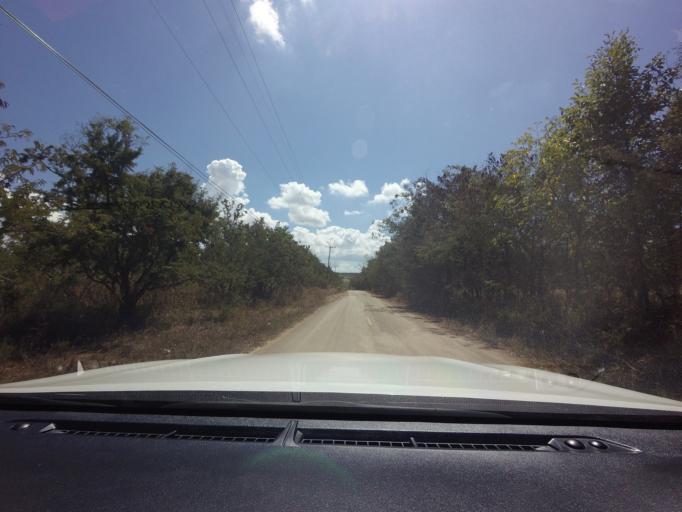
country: TH
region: Nakhon Ratchasima
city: Wang Nam Khiao
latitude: 14.4392
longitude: 101.6946
